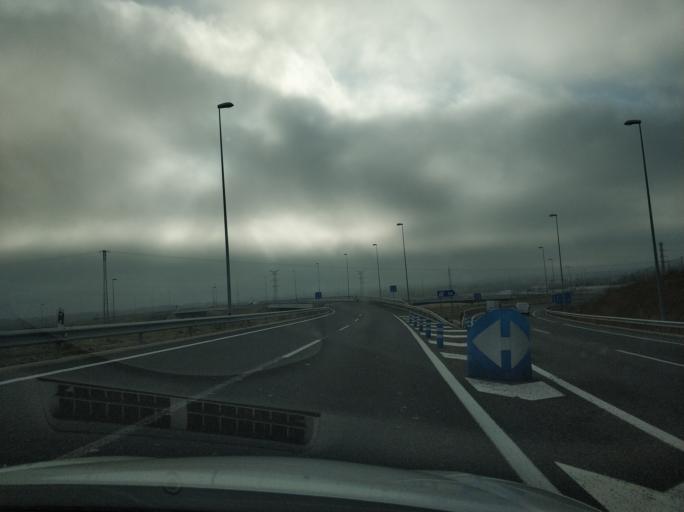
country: ES
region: Castille and Leon
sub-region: Provincia de Leon
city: Leon
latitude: 42.5719
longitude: -5.5425
